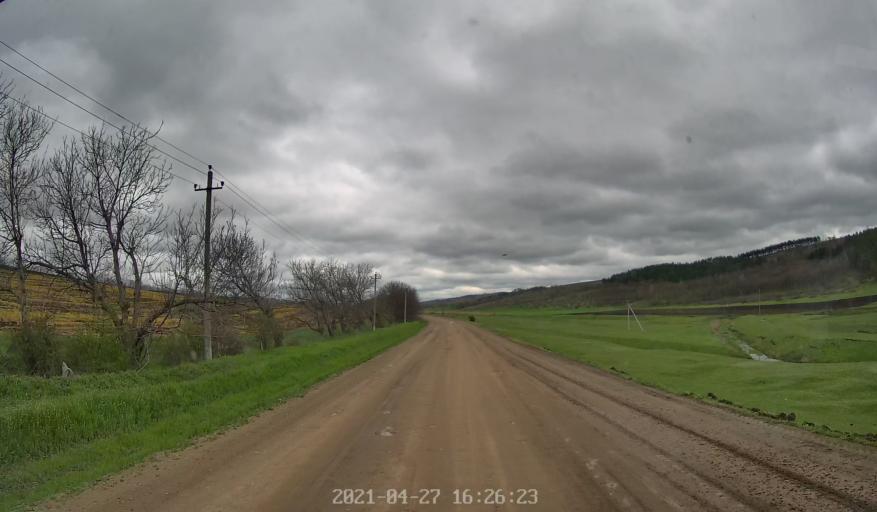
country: MD
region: Chisinau
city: Singera
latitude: 46.9800
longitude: 29.0259
